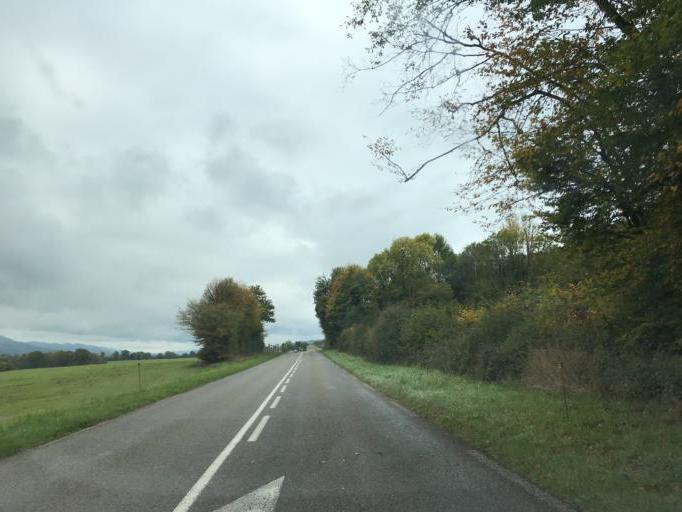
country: FR
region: Franche-Comte
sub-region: Departement du Jura
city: Arinthod
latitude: 46.4587
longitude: 5.5557
